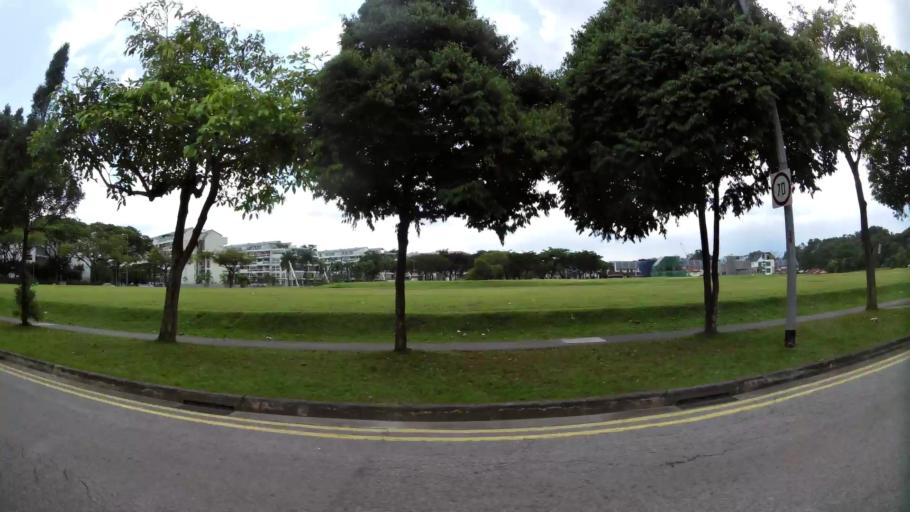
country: MY
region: Johor
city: Kampung Pasir Gudang Baru
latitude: 1.4442
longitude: 103.8228
